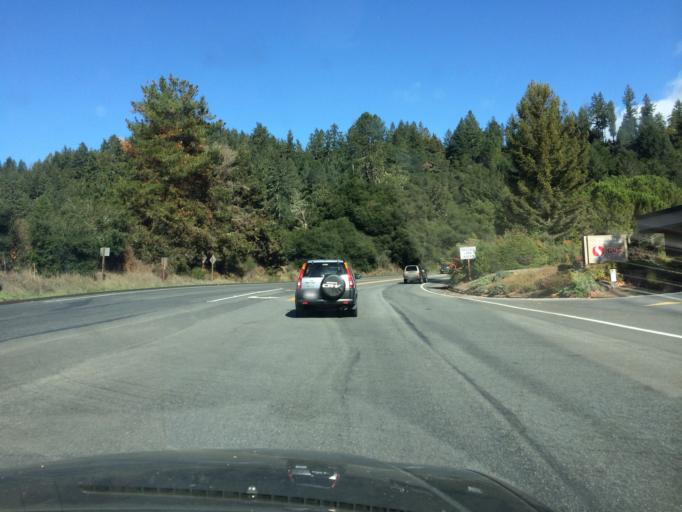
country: US
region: California
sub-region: Santa Cruz County
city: Felton
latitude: 37.0529
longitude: -122.0698
